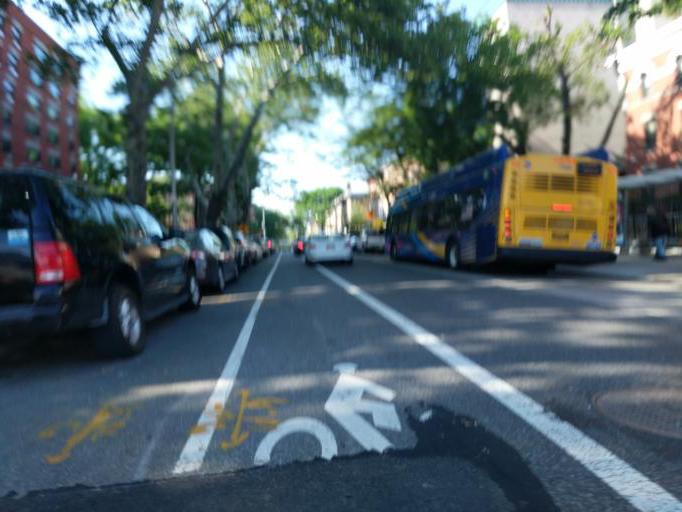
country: US
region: New York
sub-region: Kings County
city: Brooklyn
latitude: 40.6713
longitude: -73.9421
